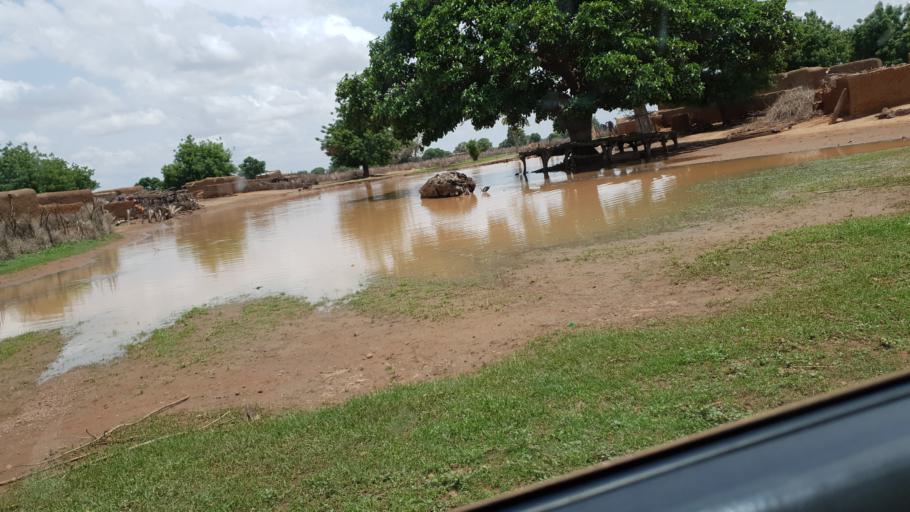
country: ML
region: Koulikoro
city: Banamba
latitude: 13.3753
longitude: -7.2222
